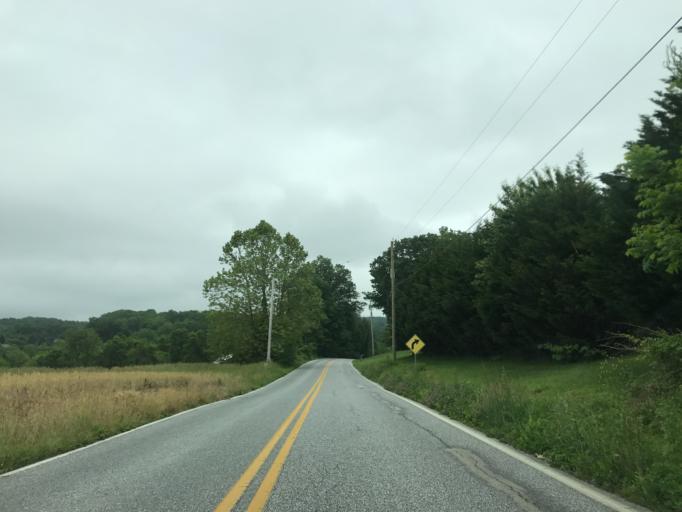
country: US
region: Pennsylvania
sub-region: York County
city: Susquehanna Trails
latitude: 39.7505
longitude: -76.4574
